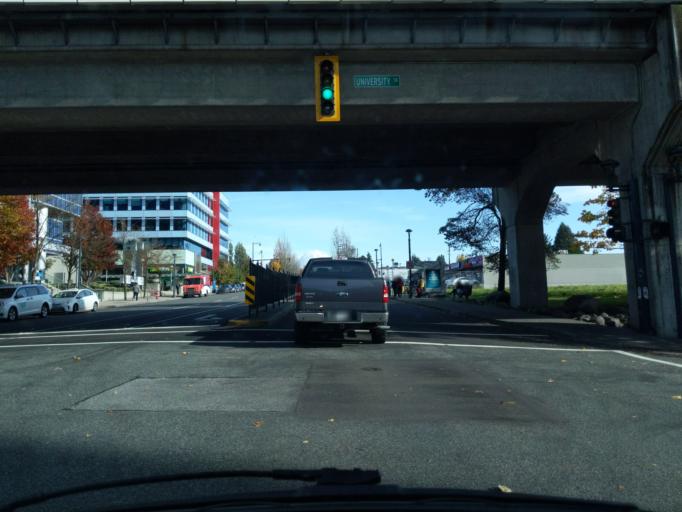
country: CA
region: British Columbia
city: New Westminster
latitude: 49.1989
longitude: -122.8509
